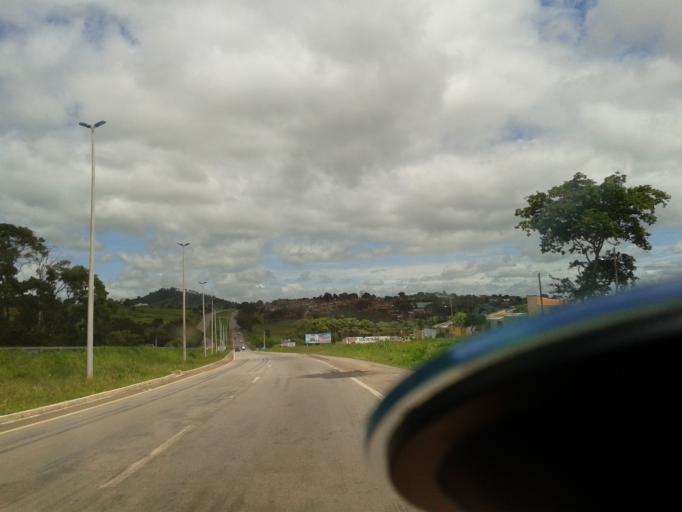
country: BR
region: Goias
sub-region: Inhumas
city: Inhumas
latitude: -16.3738
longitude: -49.5018
